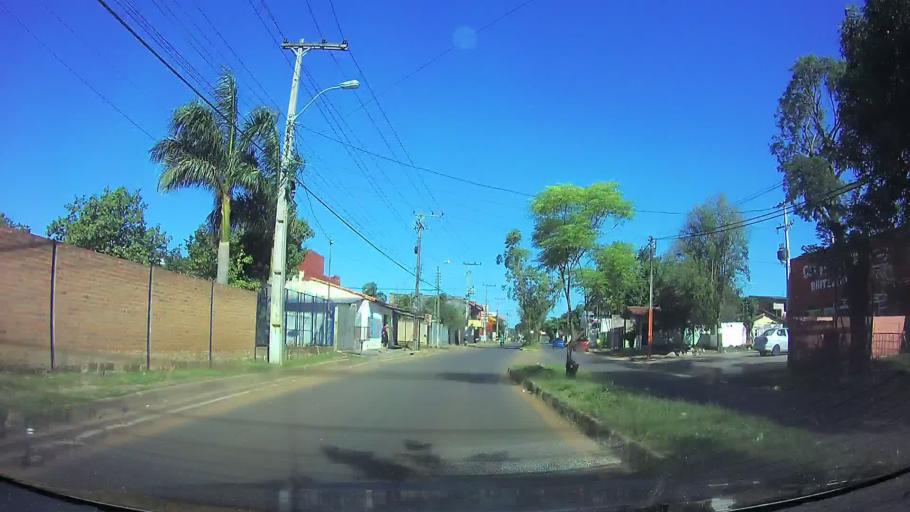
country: PY
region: Central
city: San Lorenzo
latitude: -25.2982
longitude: -57.5095
